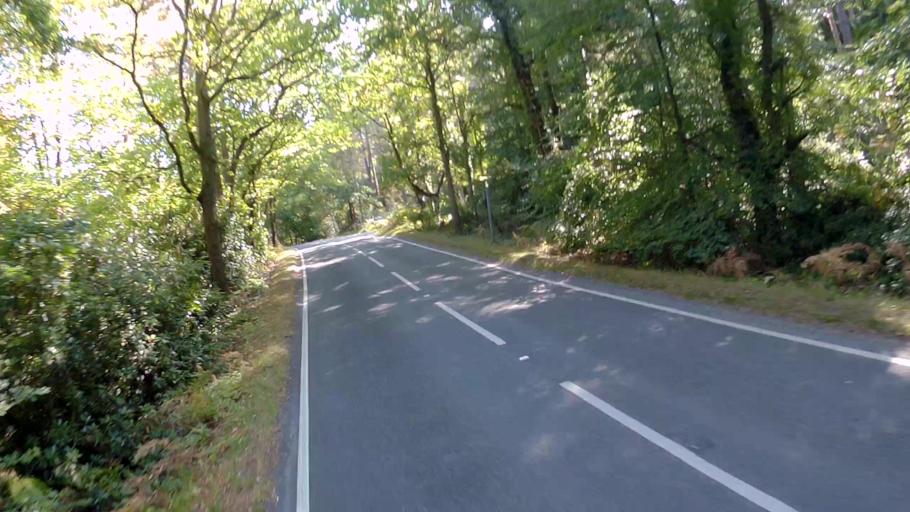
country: GB
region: England
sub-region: Surrey
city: Farnham
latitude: 51.1932
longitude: -0.7708
